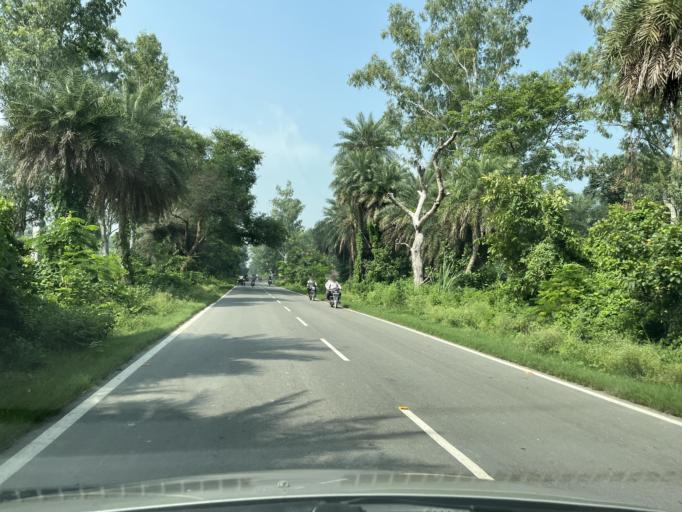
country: IN
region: Uttarakhand
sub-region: Udham Singh Nagar
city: Bazpur
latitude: 29.1783
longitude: 79.1756
